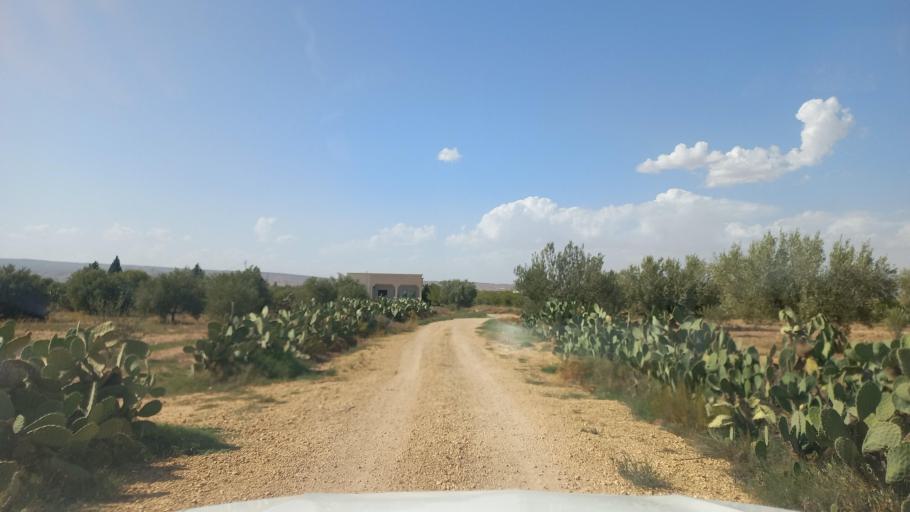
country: TN
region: Al Qasrayn
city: Sbiba
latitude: 35.3011
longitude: 9.0418
